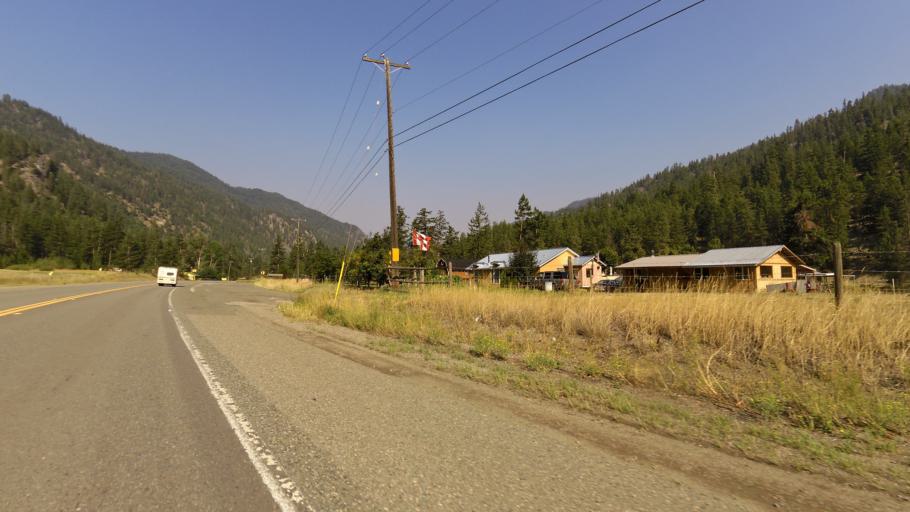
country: CA
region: British Columbia
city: Princeton
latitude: 49.3811
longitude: -120.1838
